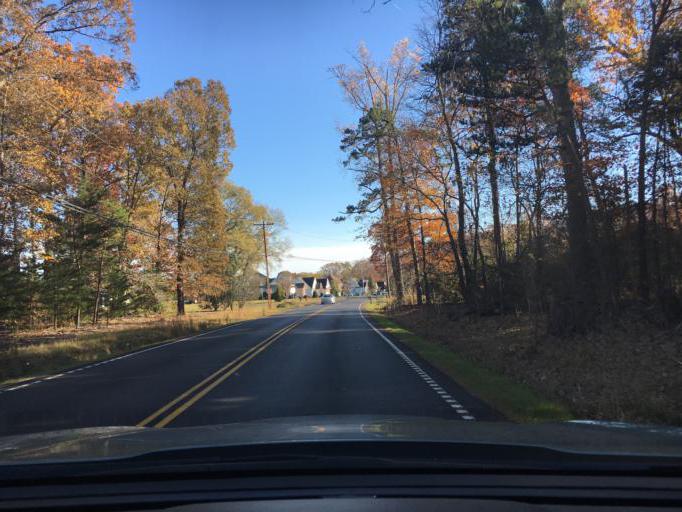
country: US
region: South Carolina
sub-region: Spartanburg County
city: Inman
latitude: 35.0130
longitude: -82.0761
